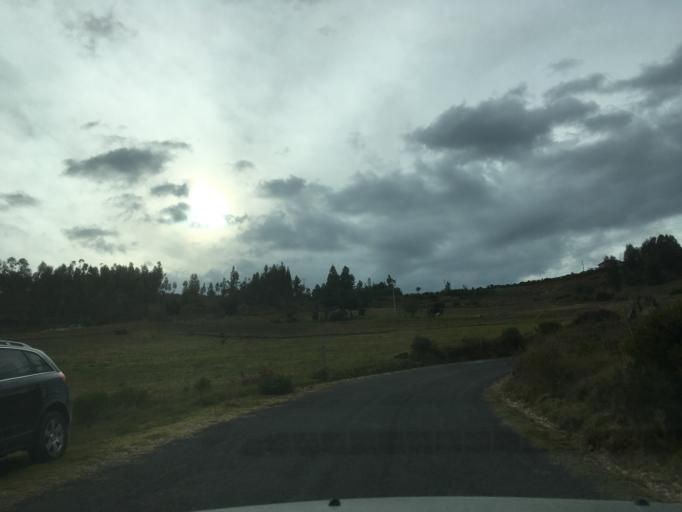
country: CO
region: Boyaca
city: Firavitoba
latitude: 5.6729
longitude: -73.0146
